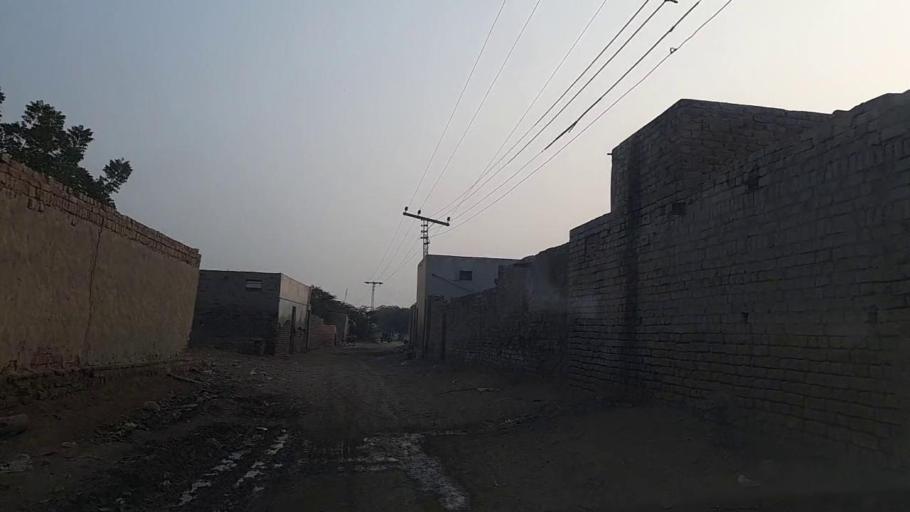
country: PK
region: Sindh
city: Sinjhoro
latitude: 26.1040
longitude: 68.7968
